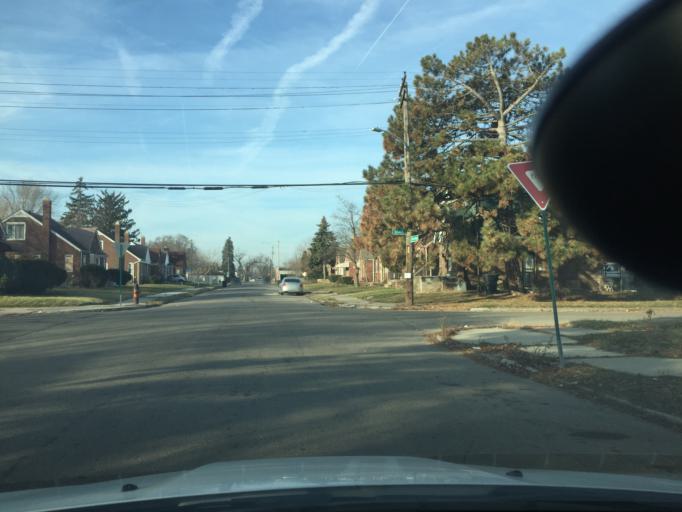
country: US
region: Michigan
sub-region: Macomb County
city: Eastpointe
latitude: 42.4332
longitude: -82.9627
